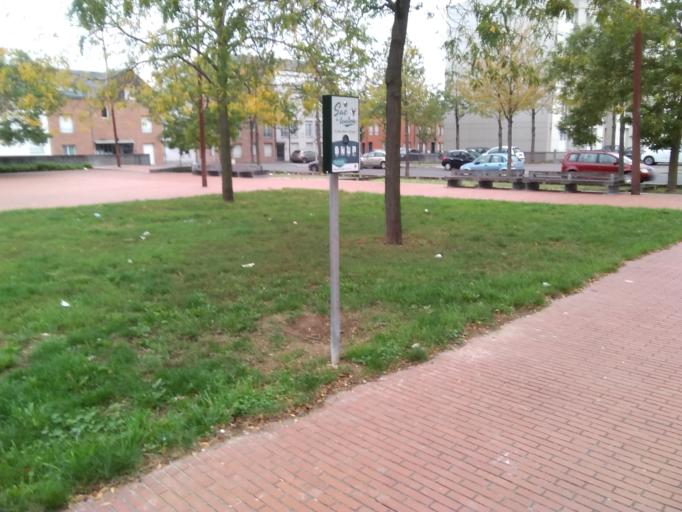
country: FR
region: Picardie
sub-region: Departement de la Somme
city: Amiens
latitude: 49.9125
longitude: 2.3007
